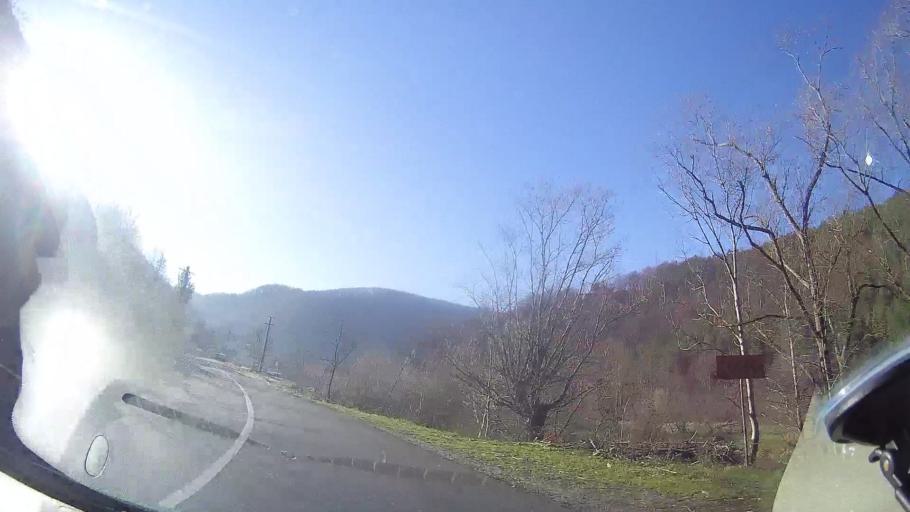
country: RO
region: Bihor
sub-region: Comuna Bulz
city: Bulz
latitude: 46.9290
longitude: 22.6591
